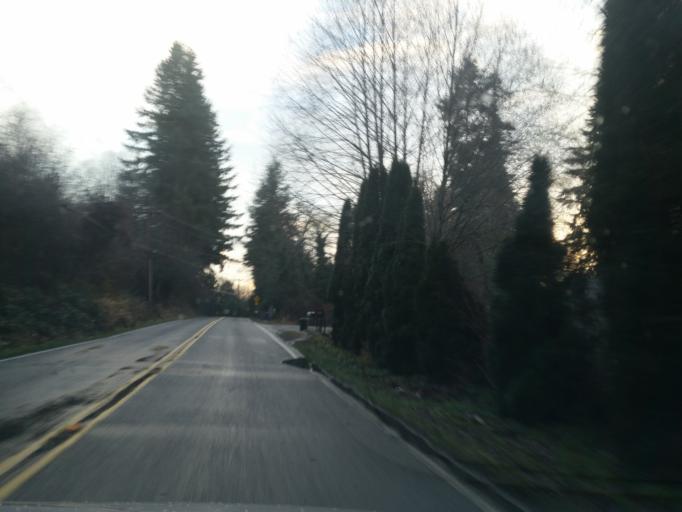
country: US
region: Washington
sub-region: Snohomish County
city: Cathcart
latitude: 47.8313
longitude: -122.0923
